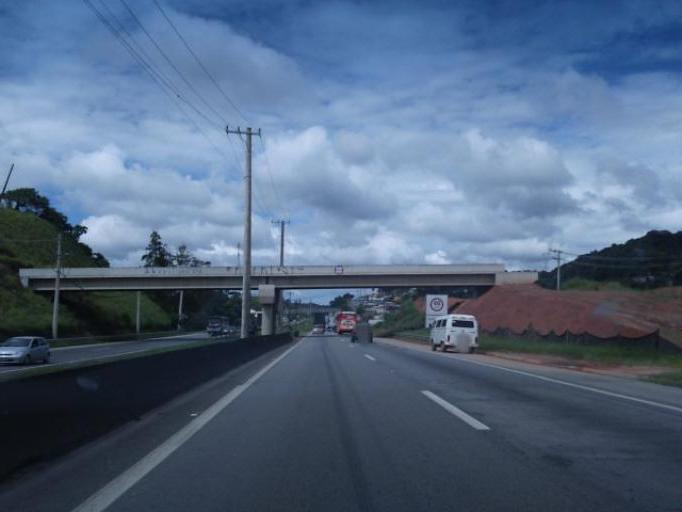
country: BR
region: Sao Paulo
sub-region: Sao Lourenco Da Serra
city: Sao Lourenco da Serra
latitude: -23.8821
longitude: -46.9726
